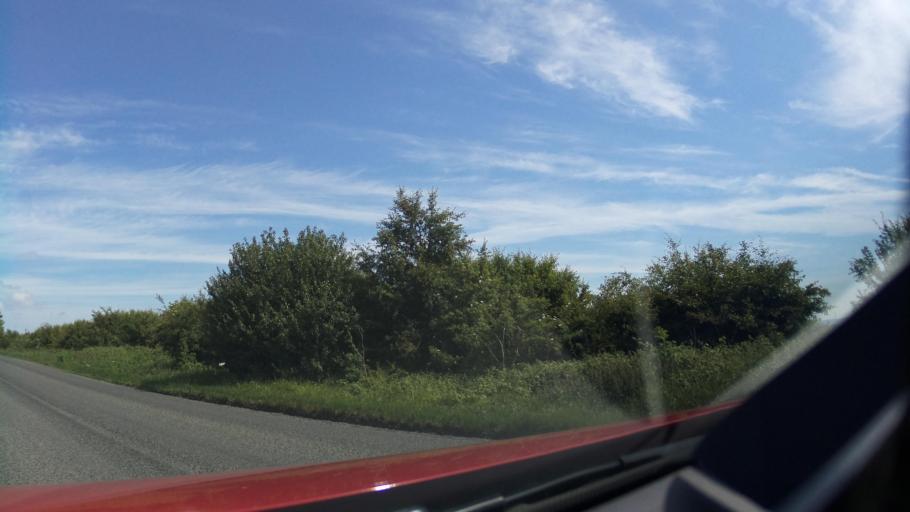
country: GB
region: England
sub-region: North Lincolnshire
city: Redbourne
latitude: 53.4239
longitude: -0.5496
